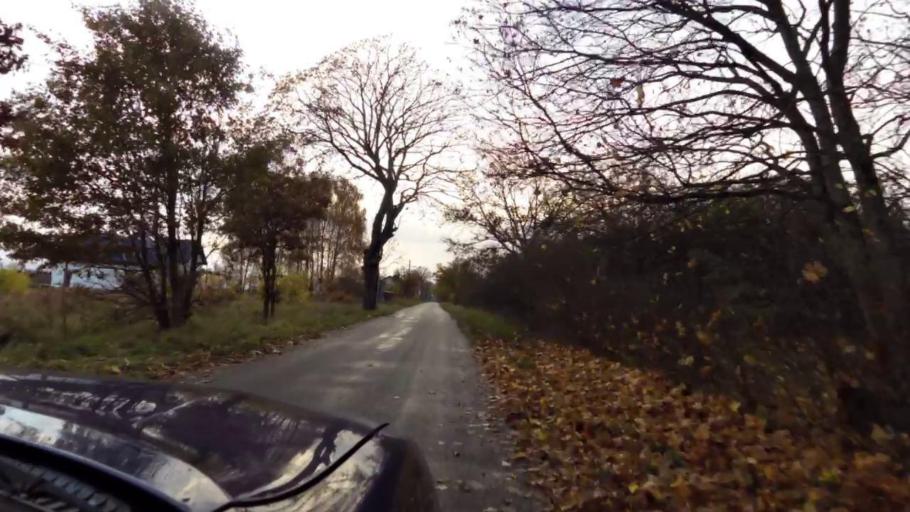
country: PL
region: West Pomeranian Voivodeship
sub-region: Powiat goleniowski
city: Goleniow
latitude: 53.5905
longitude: 14.7475
